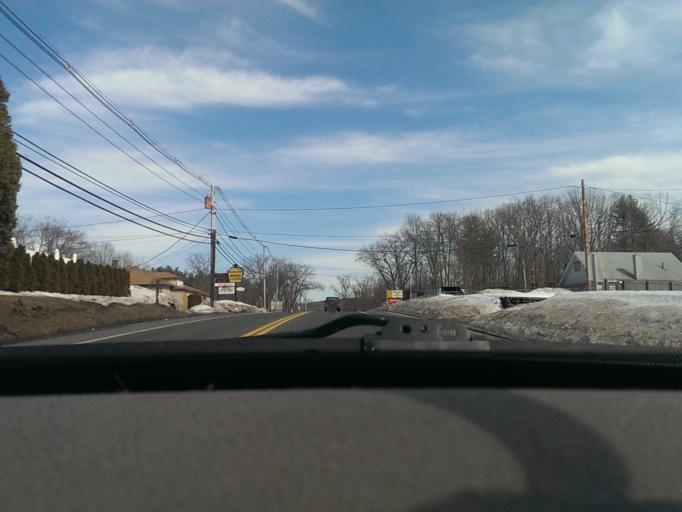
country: US
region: Massachusetts
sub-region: Hampden County
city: Three Rivers
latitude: 42.1536
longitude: -72.3731
